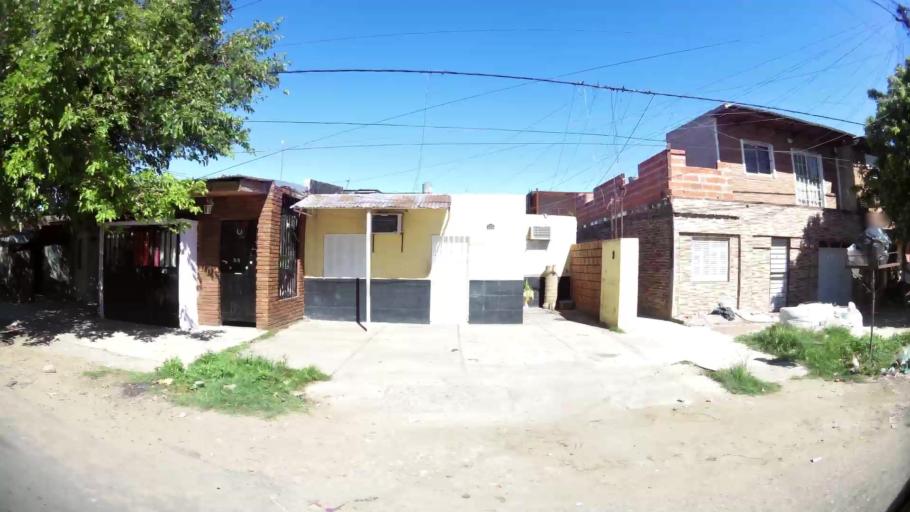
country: AR
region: Santa Fe
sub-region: Departamento de Rosario
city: Rosario
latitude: -32.9547
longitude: -60.6902
